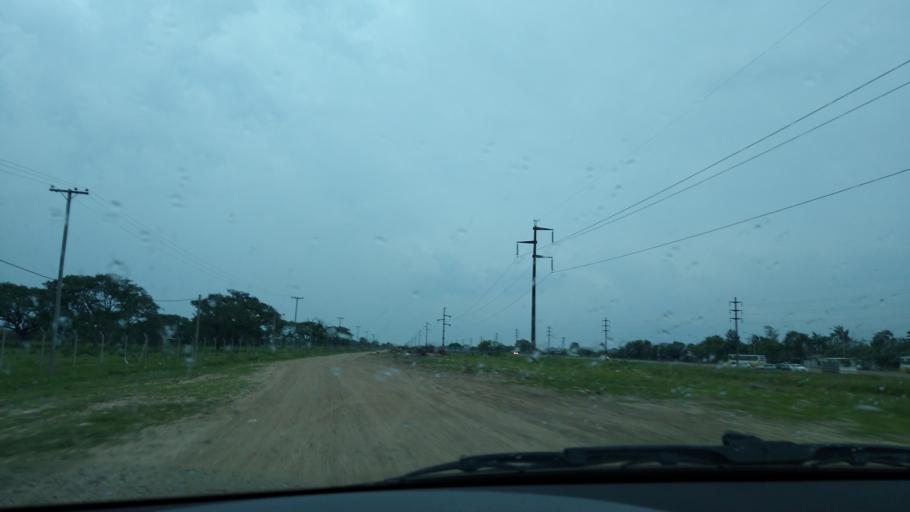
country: AR
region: Chaco
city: Resistencia
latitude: -27.4991
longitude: -58.9767
